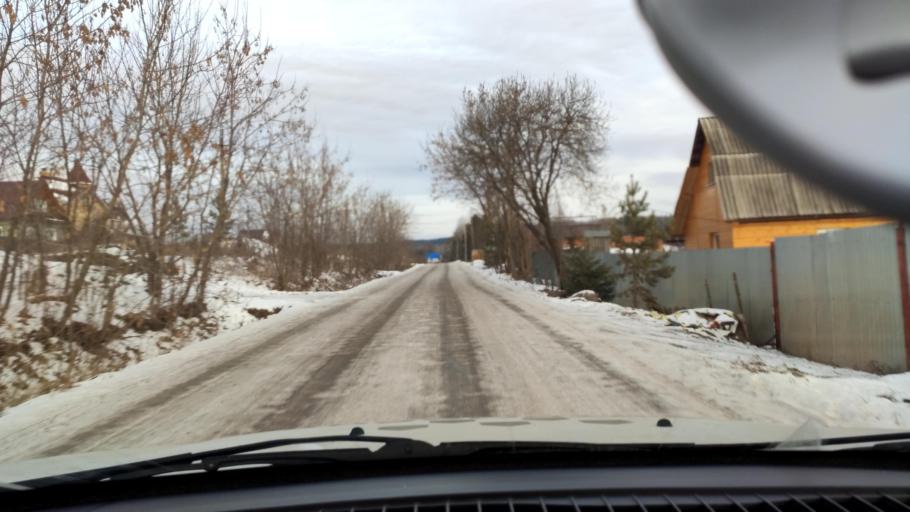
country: RU
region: Perm
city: Lobanovo
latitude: 57.8355
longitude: 56.3688
